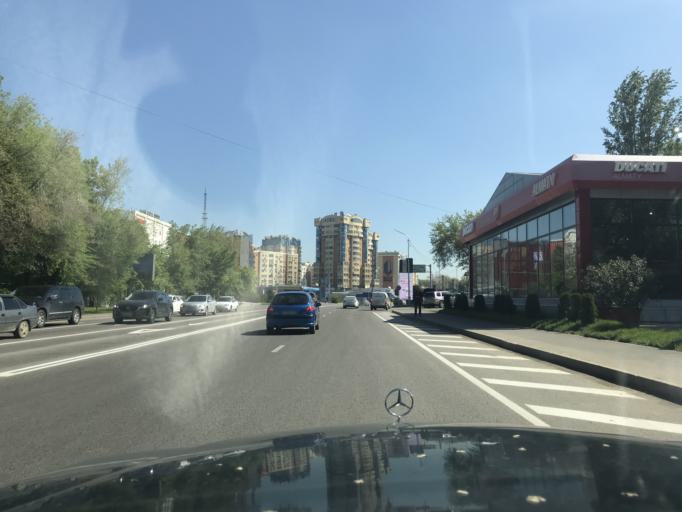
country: KZ
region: Almaty Qalasy
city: Almaty
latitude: 43.2314
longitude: 76.9346
